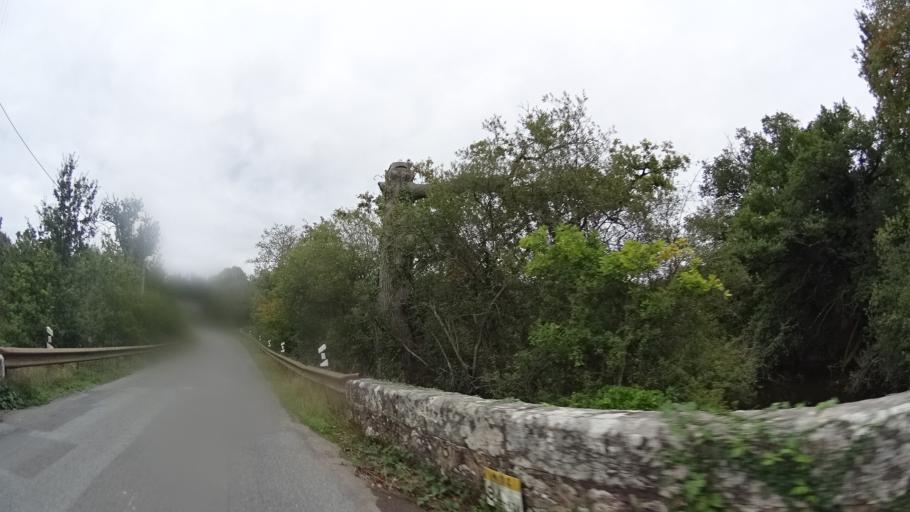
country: FR
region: Brittany
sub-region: Departement d'Ille-et-Vilaine
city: Paimpont
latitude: 48.0720
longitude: -2.1728
